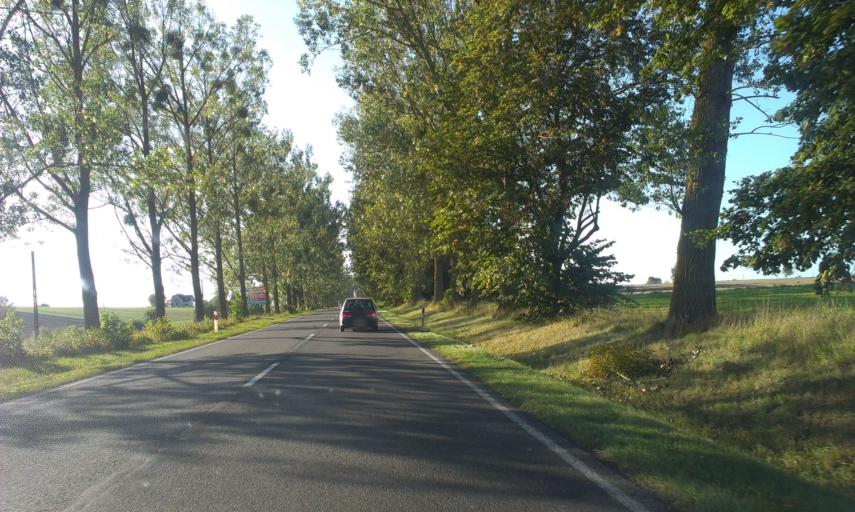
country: PL
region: Kujawsko-Pomorskie
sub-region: Powiat swiecki
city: Bukowiec
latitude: 53.4369
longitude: 18.2924
